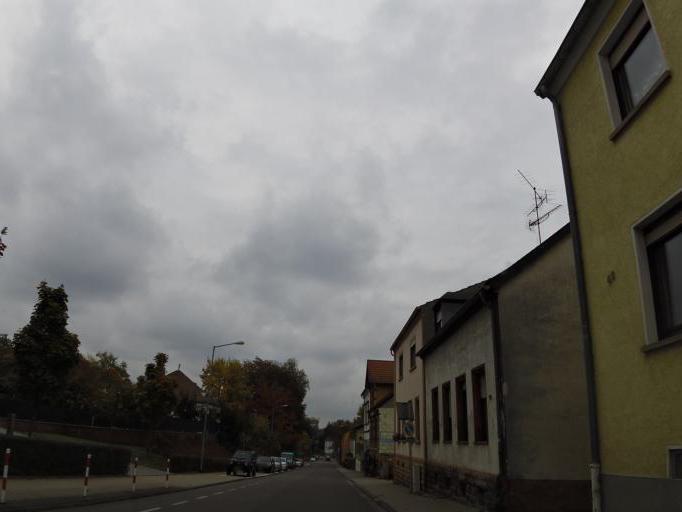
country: DE
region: Saarland
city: Sankt Ingbert
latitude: 49.2707
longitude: 7.1091
